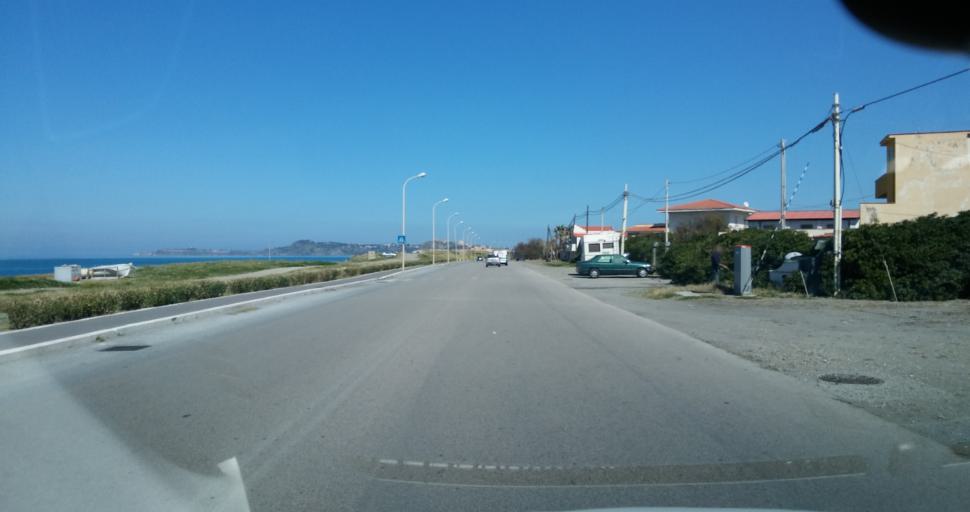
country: IT
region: Sicily
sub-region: Messina
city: Milazzo
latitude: 38.1901
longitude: 15.2164
